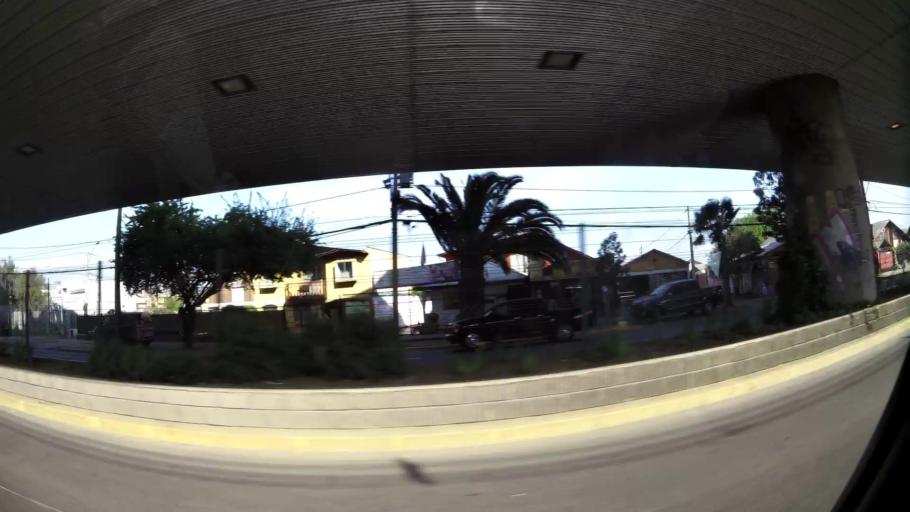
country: CL
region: Santiago Metropolitan
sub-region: Provincia de Santiago
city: Lo Prado
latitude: -33.4617
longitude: -70.7379
